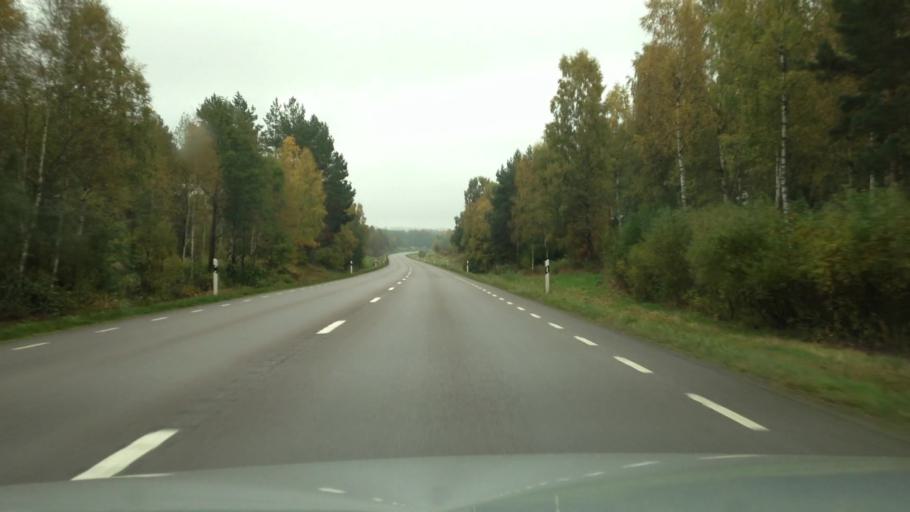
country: SE
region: Vaestra Goetaland
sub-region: Falkopings Kommun
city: Falkoeping
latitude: 58.2554
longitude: 13.5047
